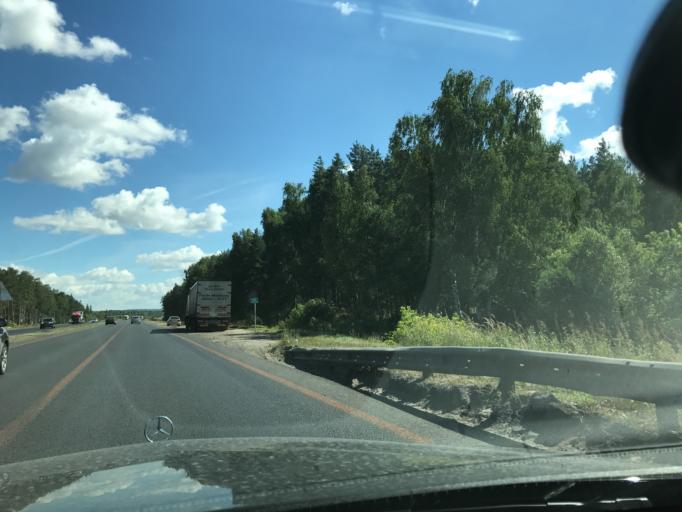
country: RU
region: Nizjnij Novgorod
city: Gorbatovka
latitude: 56.2404
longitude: 43.7284
